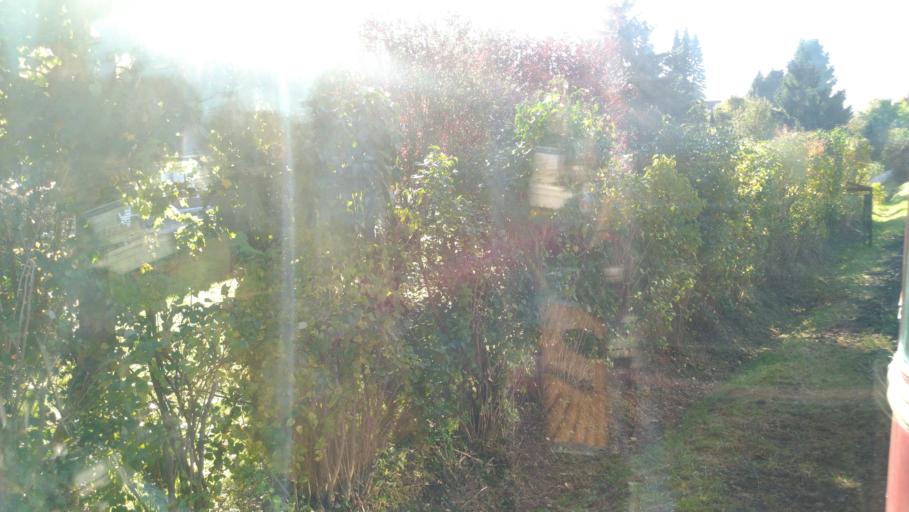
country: DE
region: Lower Saxony
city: Bad Eilsen
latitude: 52.2380
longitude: 9.1070
